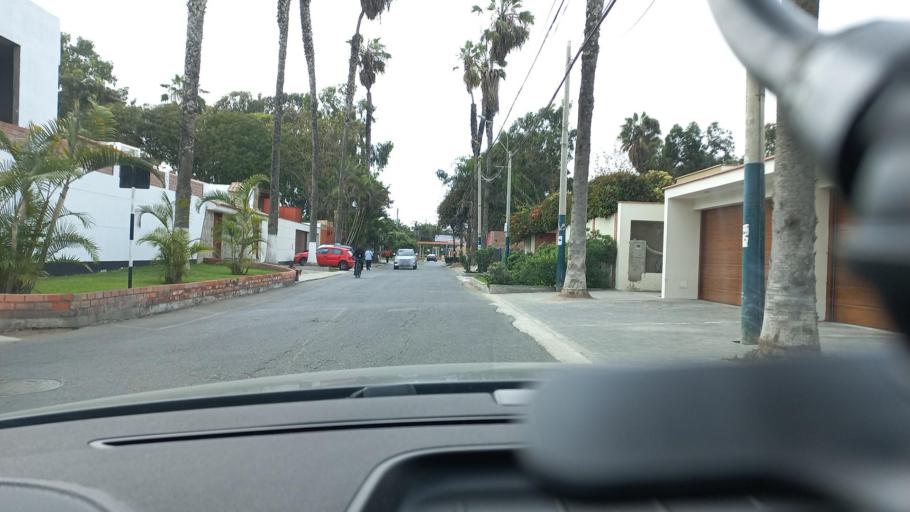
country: PE
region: Lima
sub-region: Lima
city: Surco
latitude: -12.2075
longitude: -77.0092
